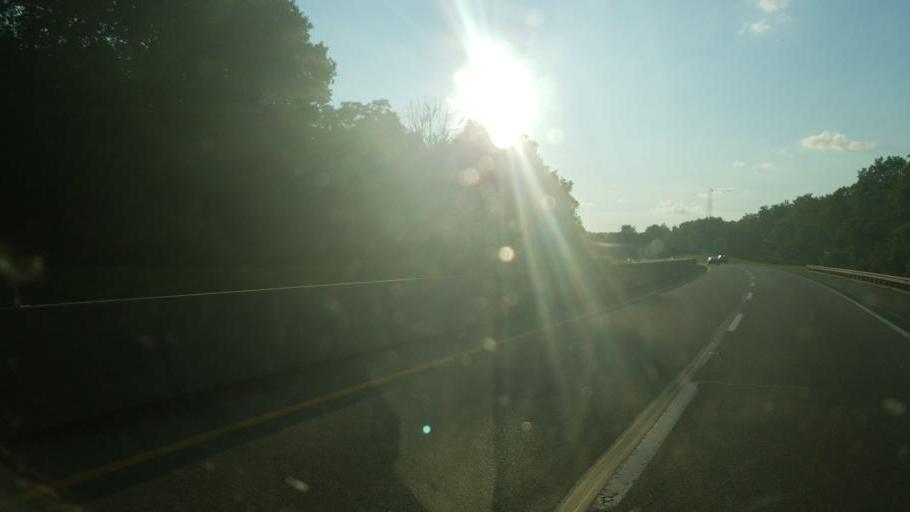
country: US
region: Pennsylvania
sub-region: Beaver County
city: Big Beaver
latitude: 40.8330
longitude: -80.3638
